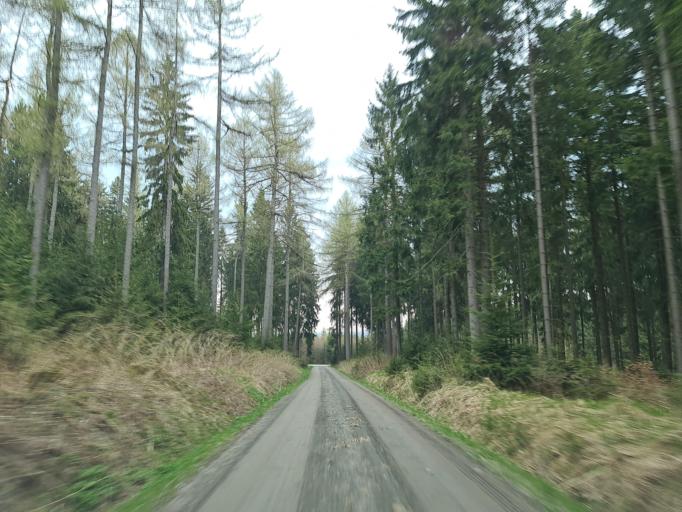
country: DE
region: Saxony
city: Ellefeld
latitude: 50.4598
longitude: 12.3992
